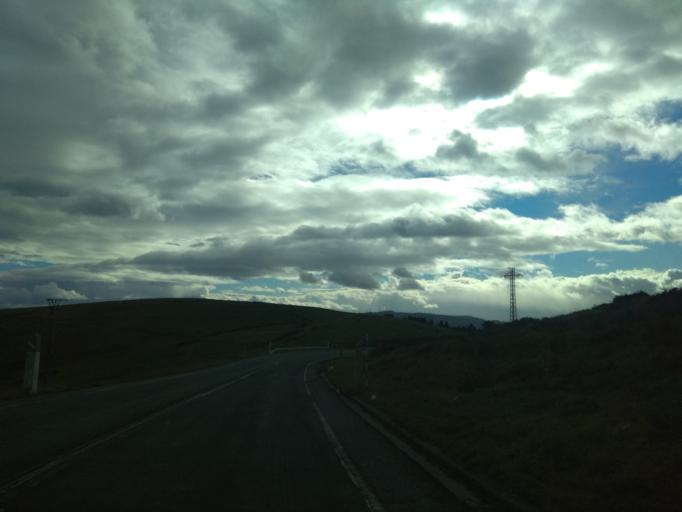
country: ES
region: Castille and Leon
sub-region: Provincia de Burgos
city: Arija
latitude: 43.0470
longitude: -3.8778
